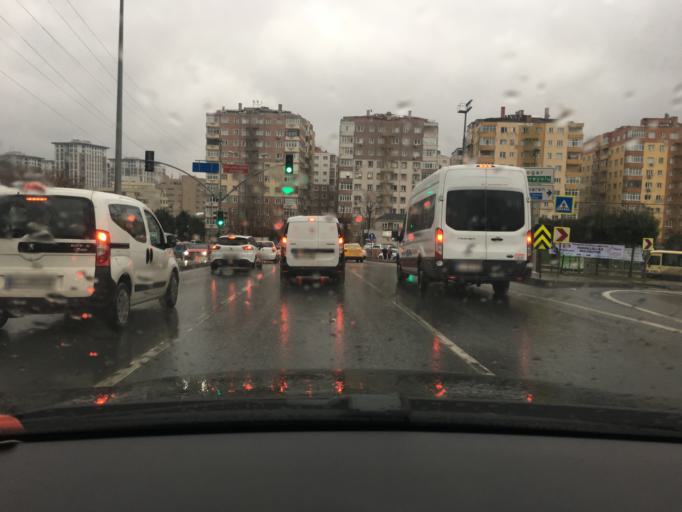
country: TR
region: Istanbul
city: merter keresteciler
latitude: 41.0188
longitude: 28.8975
